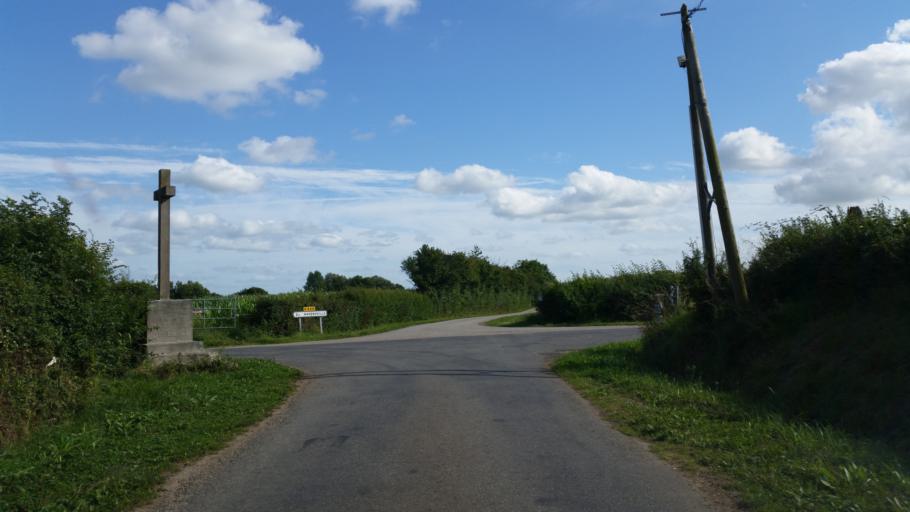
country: FR
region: Lower Normandy
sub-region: Departement de la Manche
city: Sainte-Mere-Eglise
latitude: 49.4523
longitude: -1.2914
